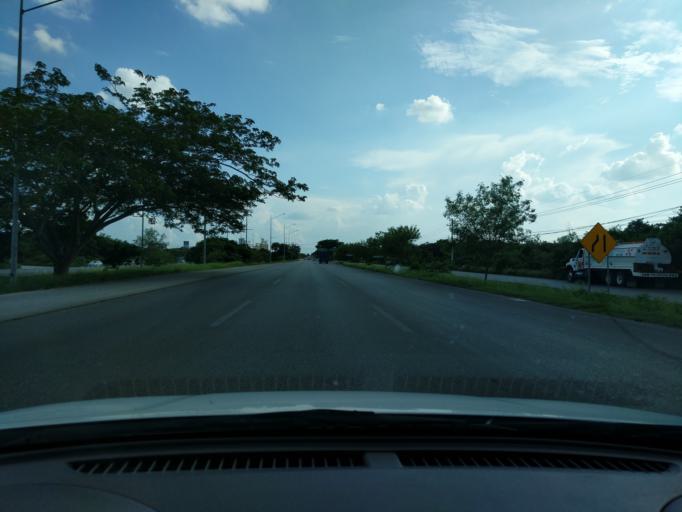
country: MX
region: Yucatan
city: Caucel
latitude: 20.9726
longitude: -89.6900
